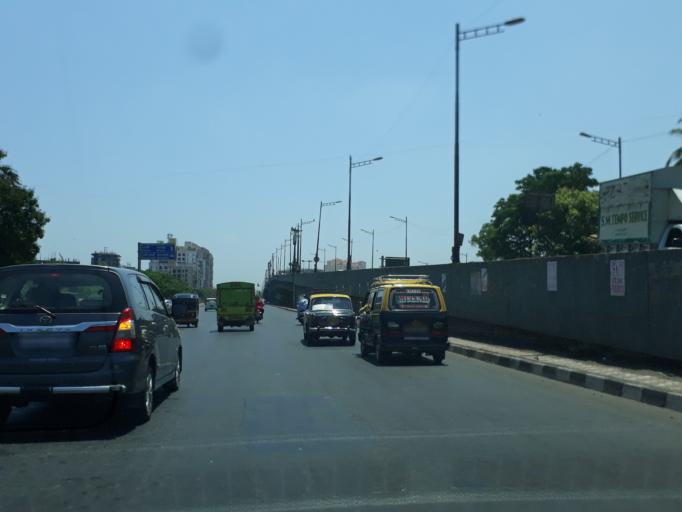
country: IN
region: Maharashtra
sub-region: Mumbai Suburban
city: Mumbai
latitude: 19.0693
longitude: 72.9048
